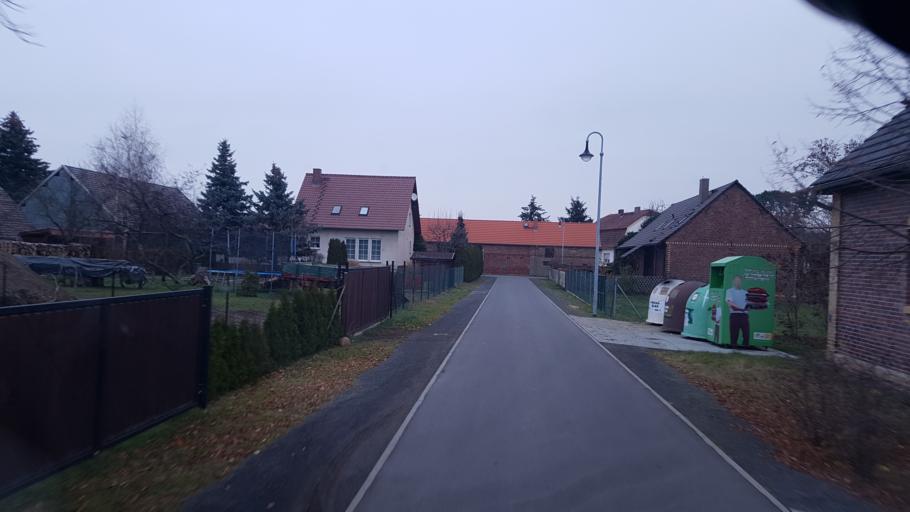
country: DE
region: Brandenburg
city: Peitz
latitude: 51.8847
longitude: 14.4173
